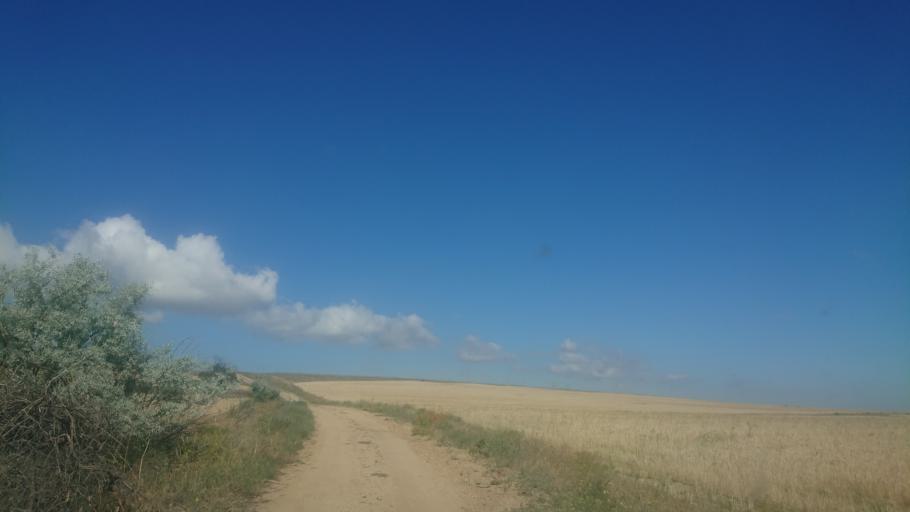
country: TR
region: Aksaray
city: Agacoren
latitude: 38.9102
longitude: 33.8763
